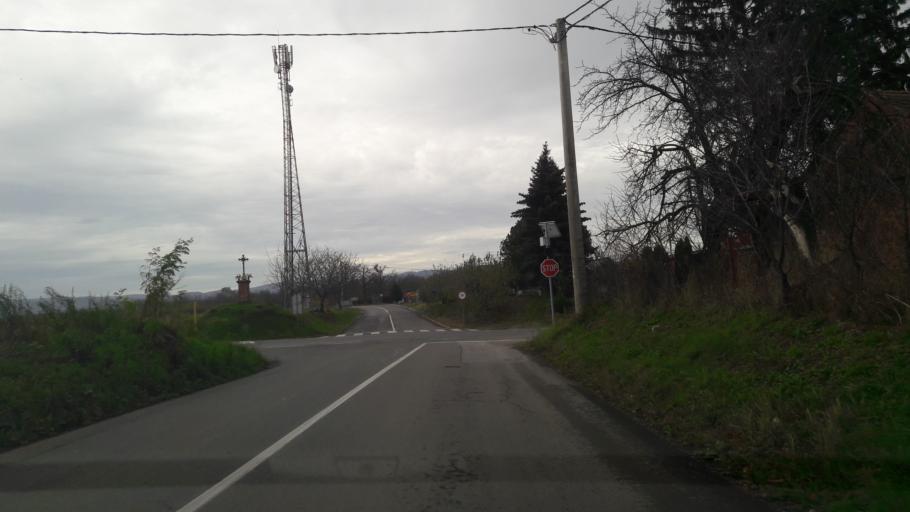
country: HR
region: Osjecko-Baranjska
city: Fericanci
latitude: 45.5200
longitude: 18.0056
